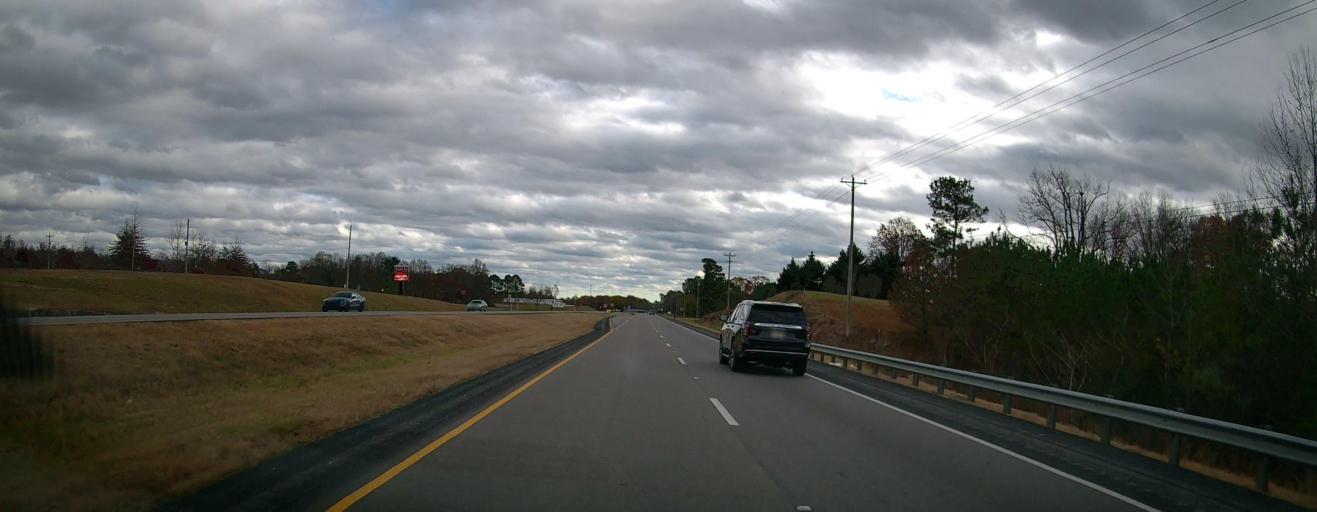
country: US
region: Alabama
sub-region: Morgan County
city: Falkville
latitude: 34.2725
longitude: -86.9929
